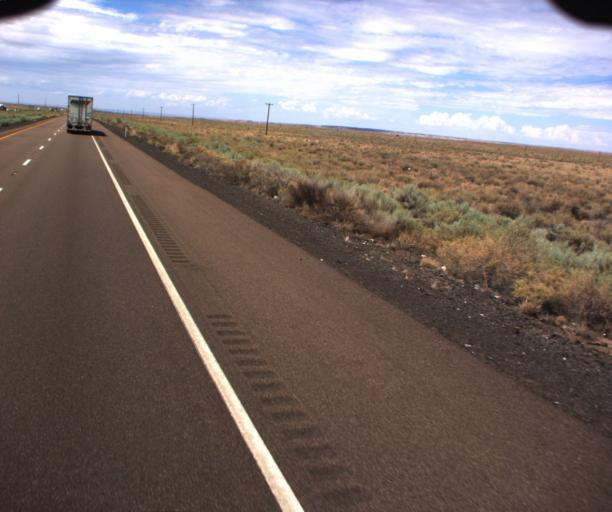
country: US
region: Arizona
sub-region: Navajo County
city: Holbrook
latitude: 35.0471
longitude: -109.8047
